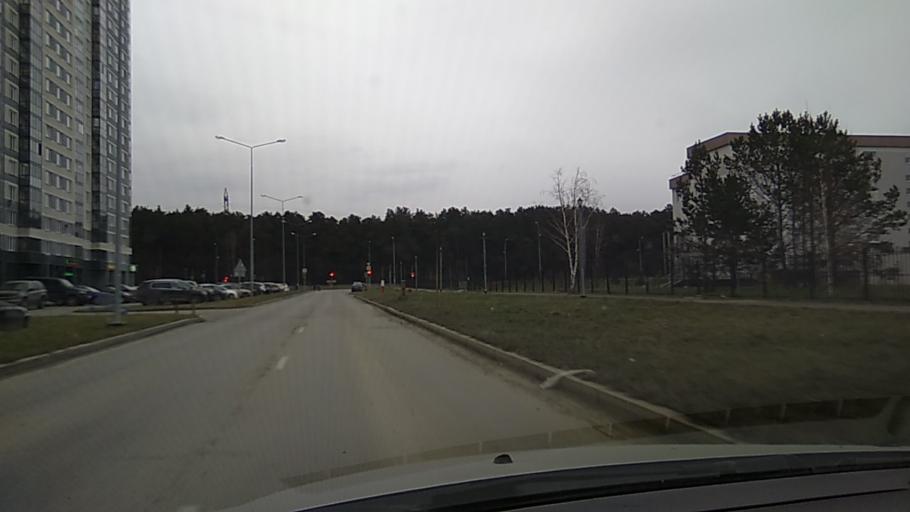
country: RU
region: Sverdlovsk
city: Sovkhoznyy
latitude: 56.7814
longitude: 60.5530
